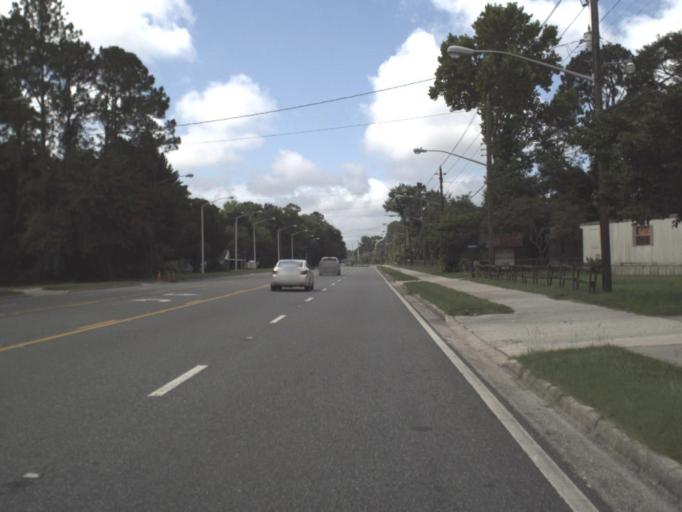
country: US
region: Florida
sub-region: Columbia County
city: Five Points
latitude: 30.2292
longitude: -82.6386
